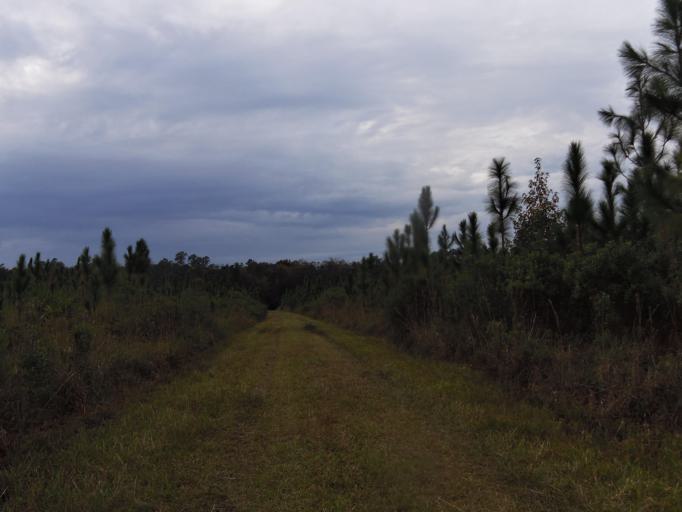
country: US
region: Florida
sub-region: Putnam County
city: Palatka
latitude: 29.6845
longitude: -81.7410
